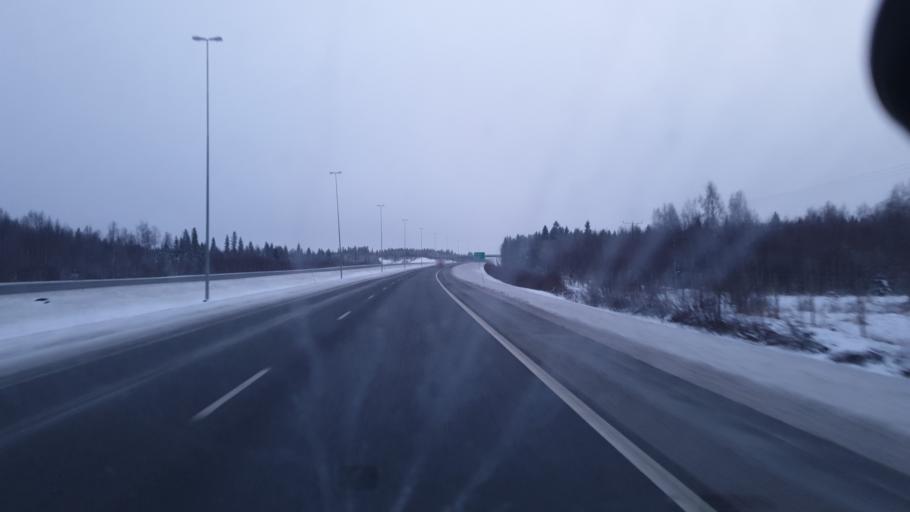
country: FI
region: Lapland
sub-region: Kemi-Tornio
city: Keminmaa
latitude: 65.8250
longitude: 24.4591
